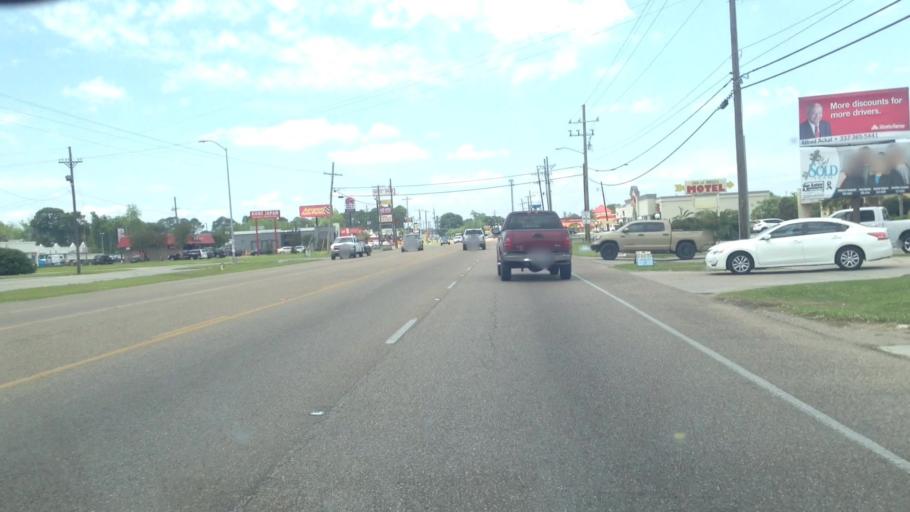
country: US
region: Louisiana
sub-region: Iberia Parish
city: New Iberia
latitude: 29.9865
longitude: -91.8222
